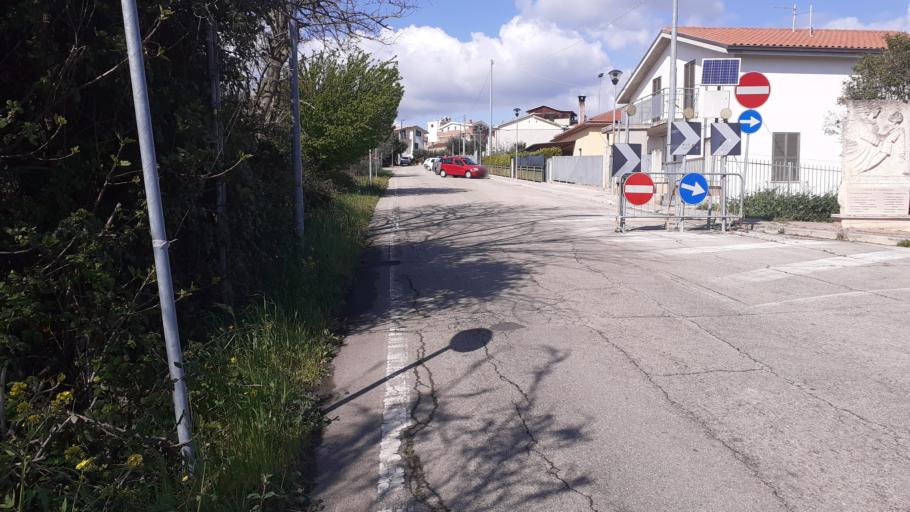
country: IT
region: Abruzzo
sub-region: Provincia di Pescara
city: Cerratina
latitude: 42.3966
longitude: 14.1103
